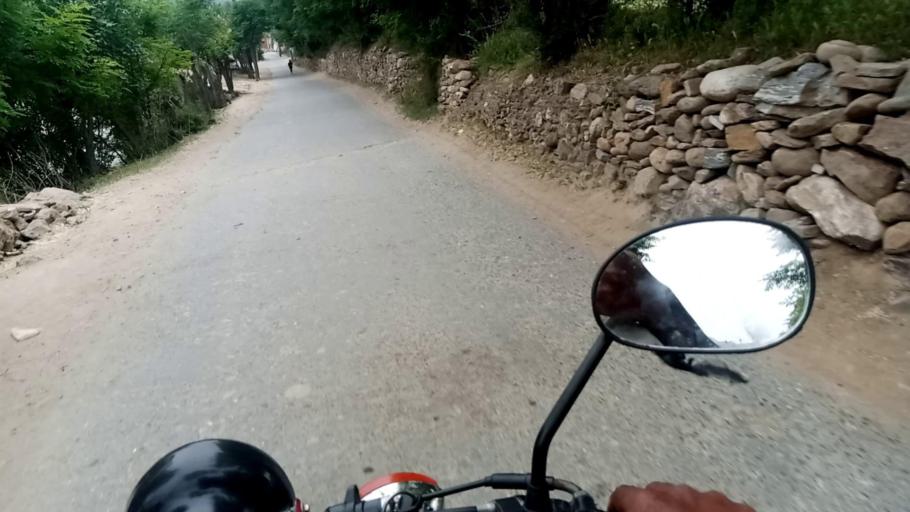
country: PK
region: Khyber Pakhtunkhwa
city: Saidu Sharif
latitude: 34.7550
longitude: 72.3785
